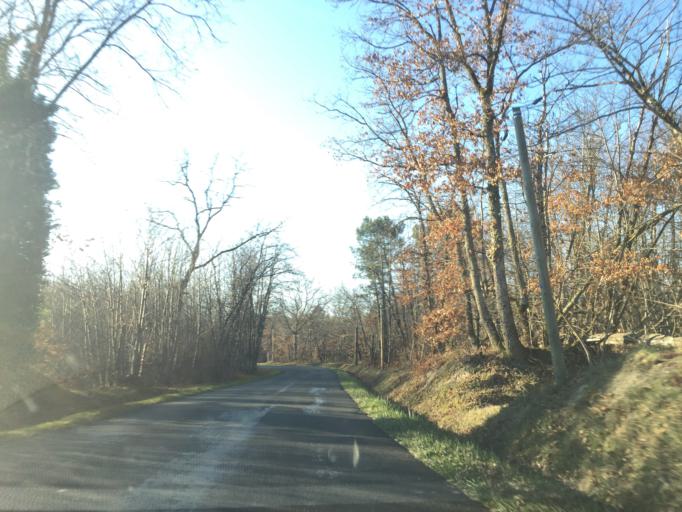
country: FR
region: Aquitaine
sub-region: Departement de la Dordogne
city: Riberac
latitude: 45.2039
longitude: 0.3481
